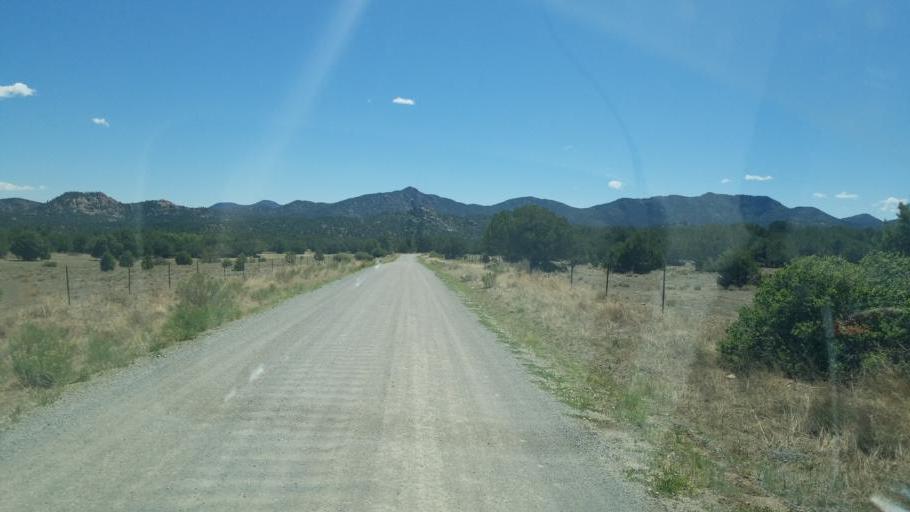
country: US
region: Colorado
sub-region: Custer County
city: Westcliffe
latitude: 38.3055
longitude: -105.6193
